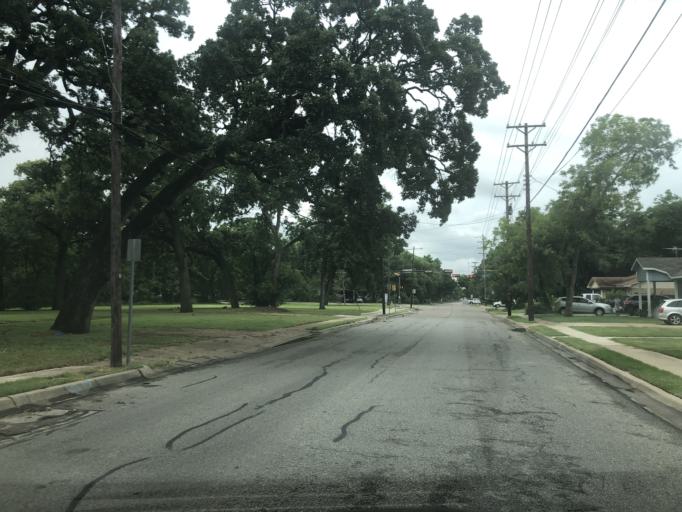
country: US
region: Texas
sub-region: Dallas County
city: Irving
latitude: 32.8095
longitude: -96.9425
